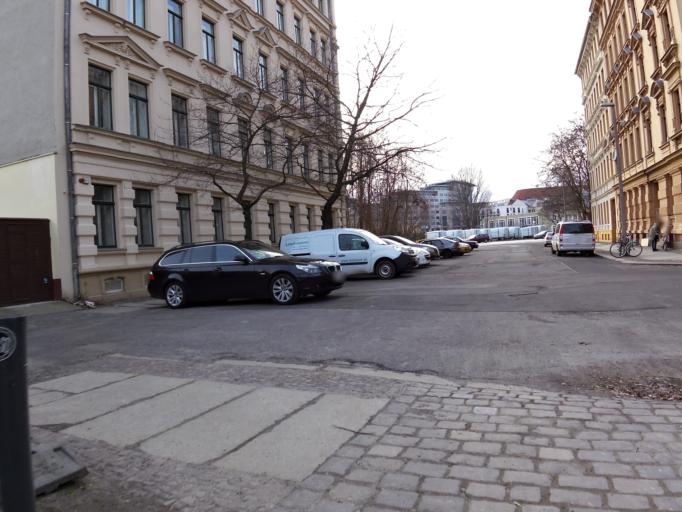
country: DE
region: Saxony
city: Leipzig
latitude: 51.3452
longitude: 12.3968
